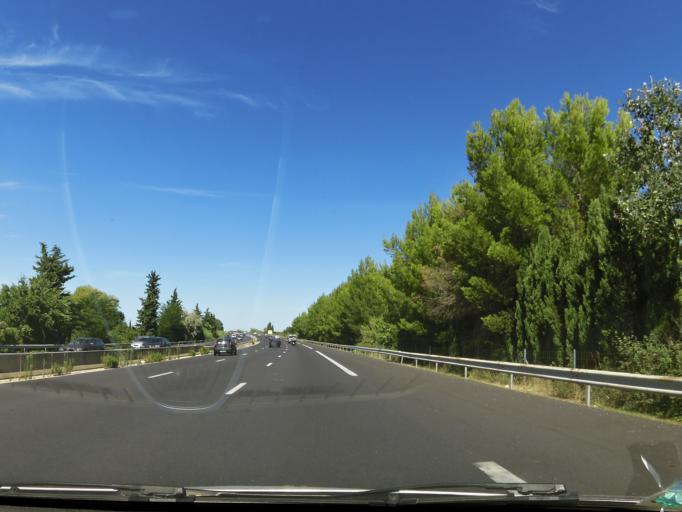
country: FR
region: Languedoc-Roussillon
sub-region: Departement du Gard
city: Rodilhan
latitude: 43.8384
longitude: 4.4120
